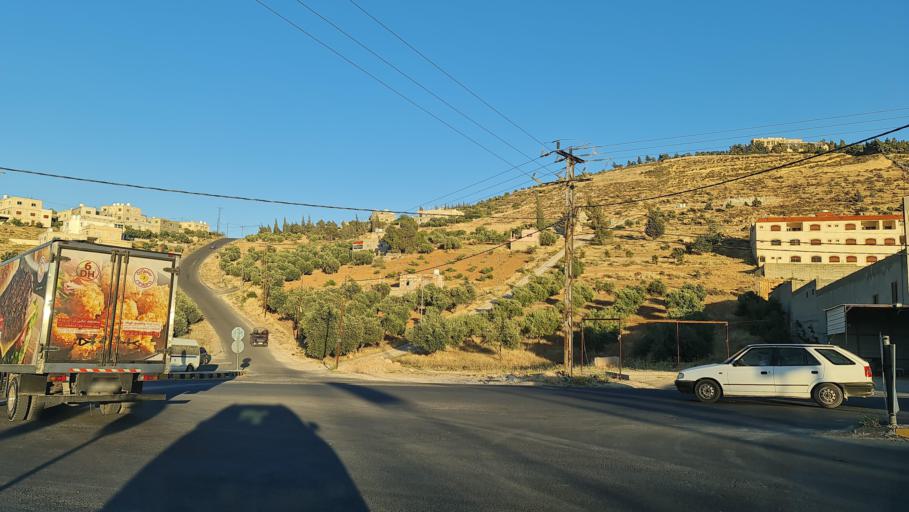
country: JO
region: Amman
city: Al Jubayhah
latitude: 32.0912
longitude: 35.9356
